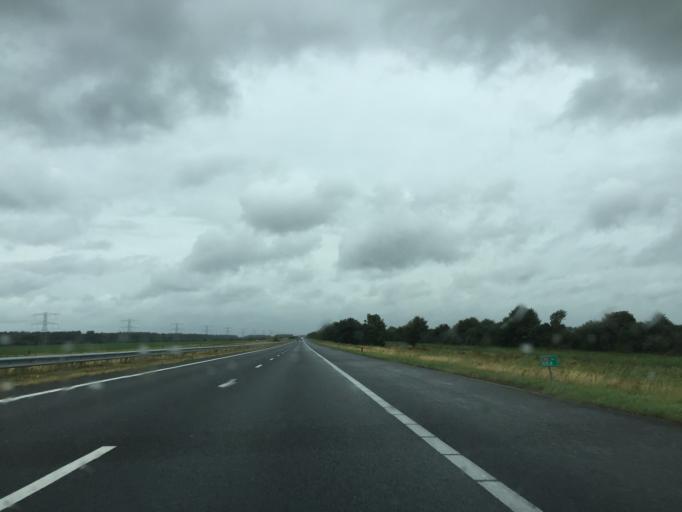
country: NL
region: Flevoland
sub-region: Gemeente Lelystad
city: Lelystad
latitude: 52.4458
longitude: 5.4426
